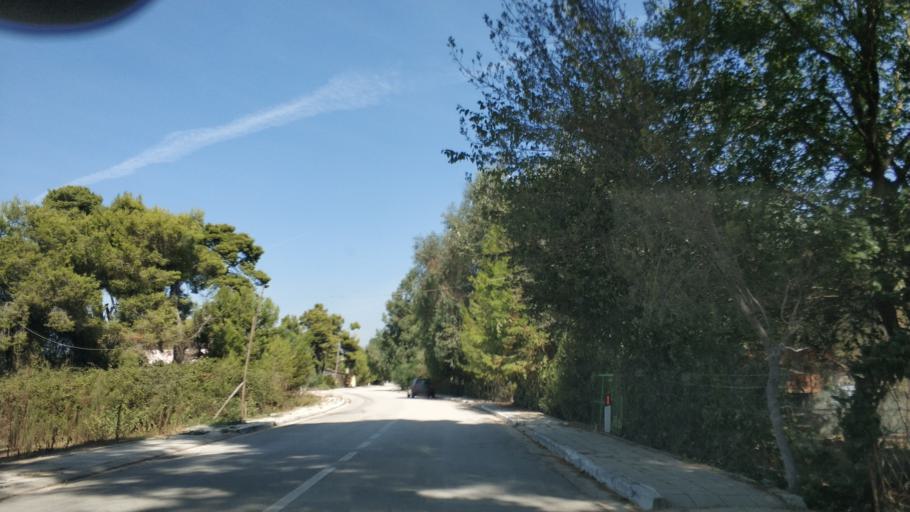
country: AL
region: Fier
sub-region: Rrethi i Lushnjes
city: Divjake
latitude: 40.9655
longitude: 19.4781
